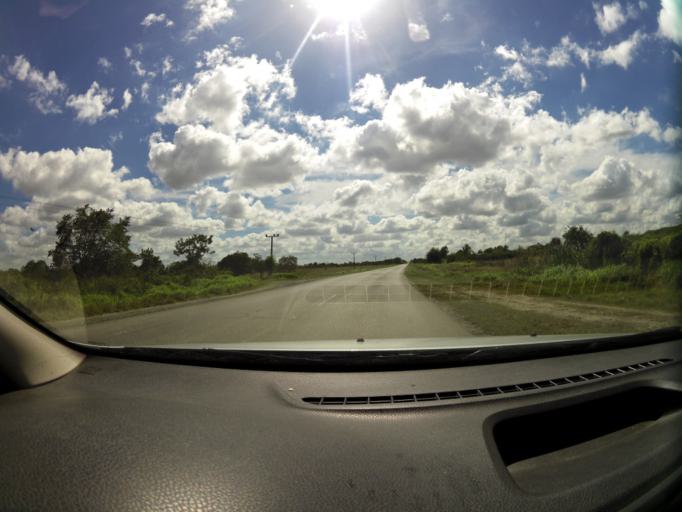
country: CU
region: Las Tunas
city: Las Tunas
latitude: 20.8945
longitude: -76.9132
